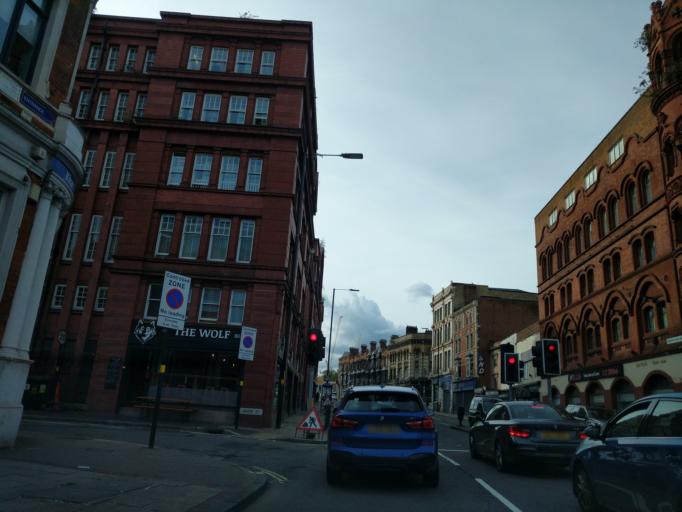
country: GB
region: England
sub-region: City and Borough of Birmingham
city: Birmingham
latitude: 52.4864
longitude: -1.9012
